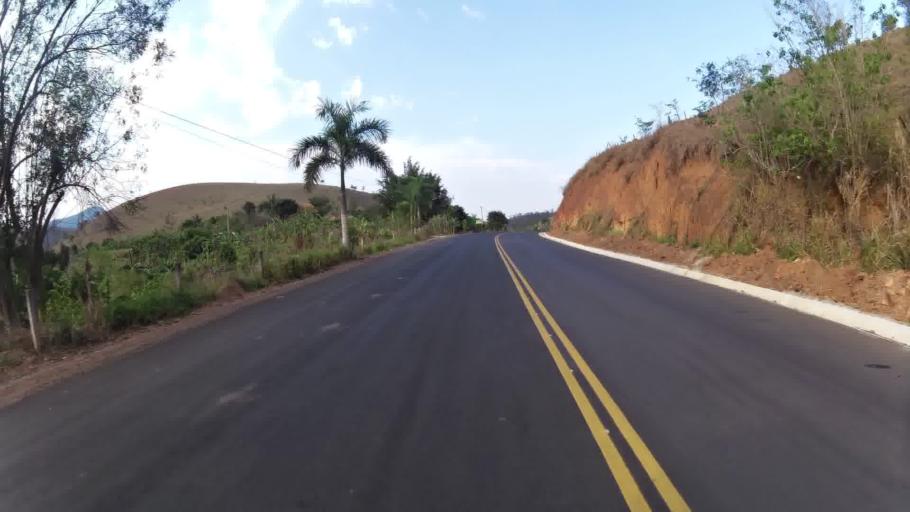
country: BR
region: Rio de Janeiro
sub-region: Santo Antonio De Padua
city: Santo Antonio de Padua
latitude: -21.4887
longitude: -42.0650
